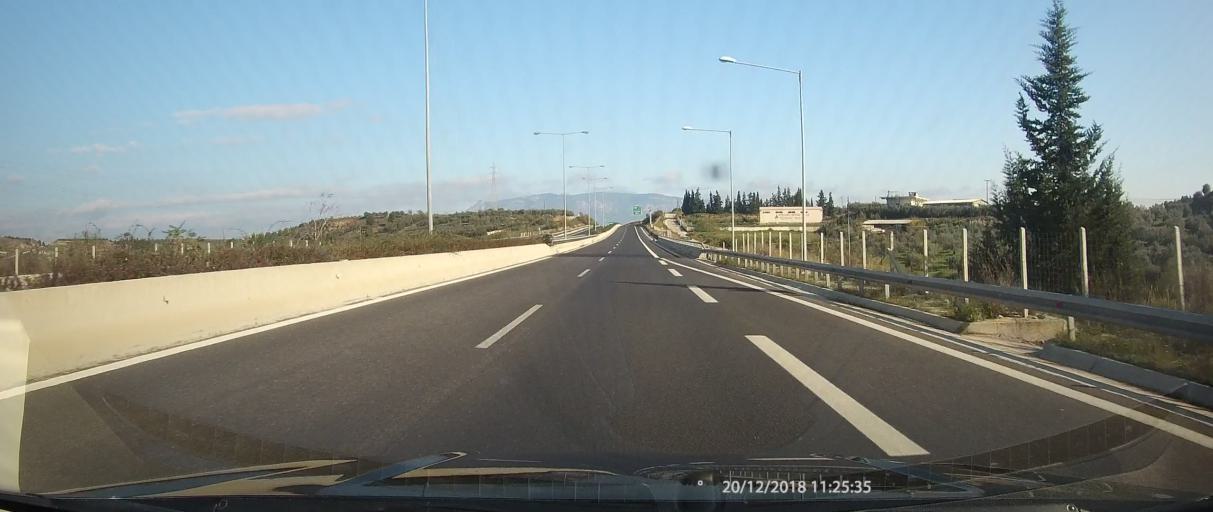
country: GR
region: Peloponnese
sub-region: Nomos Korinthias
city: Arkhaia Korinthos
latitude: 37.9006
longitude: 22.9007
